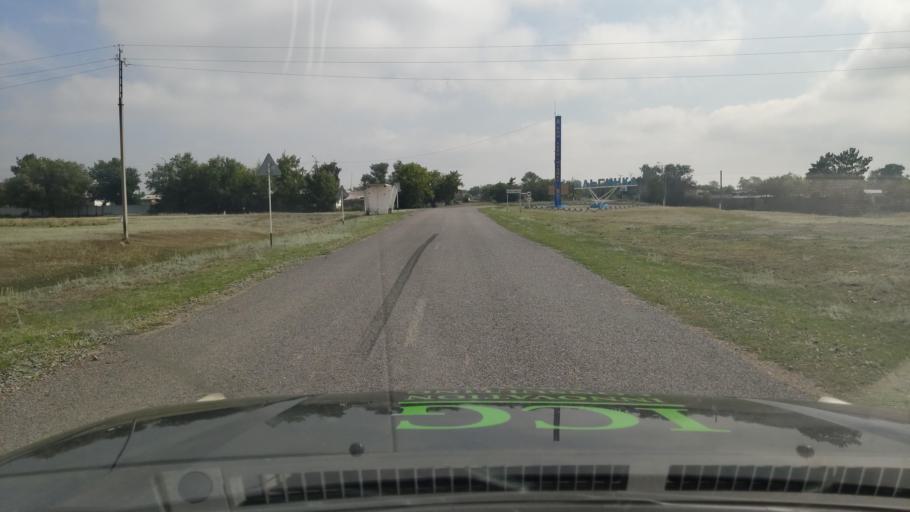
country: KZ
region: Pavlodar
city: Koktobe
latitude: 51.9647
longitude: 77.6302
